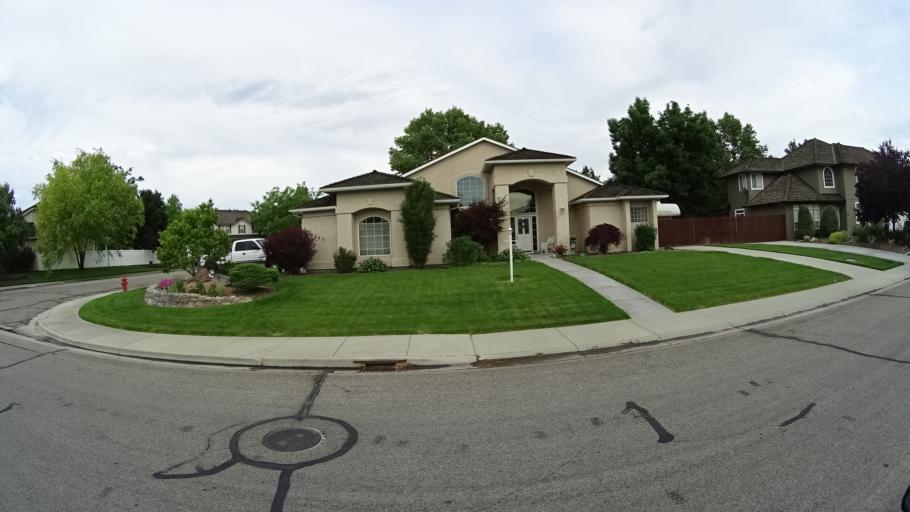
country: US
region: Idaho
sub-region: Ada County
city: Meridian
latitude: 43.5844
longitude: -116.3877
